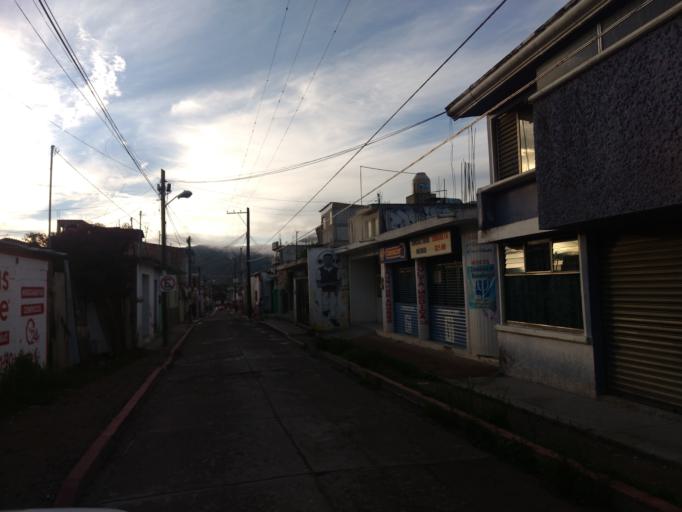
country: MX
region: Oaxaca
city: Ciudad de Huajuapam de Leon
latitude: 17.8092
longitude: -97.7782
